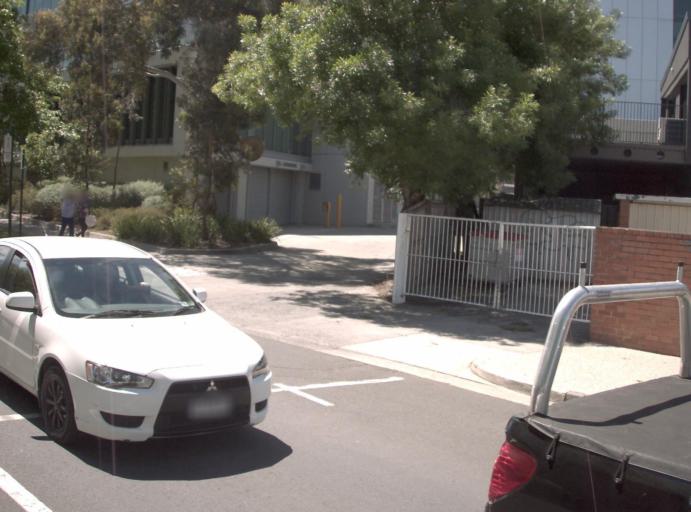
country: AU
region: Victoria
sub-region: Whitehorse
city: Blackburn
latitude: -37.8189
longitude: 145.1539
